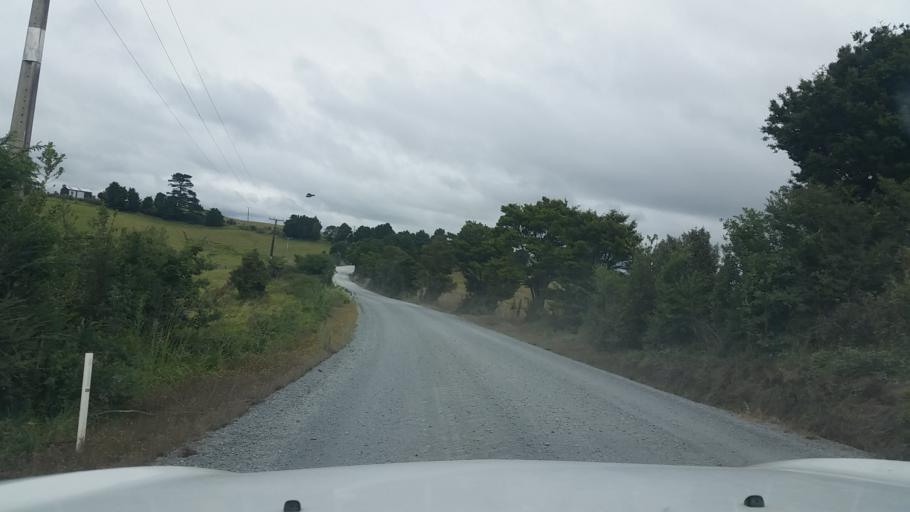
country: NZ
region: Northland
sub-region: Whangarei
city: Maungatapere
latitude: -35.6655
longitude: 174.1774
